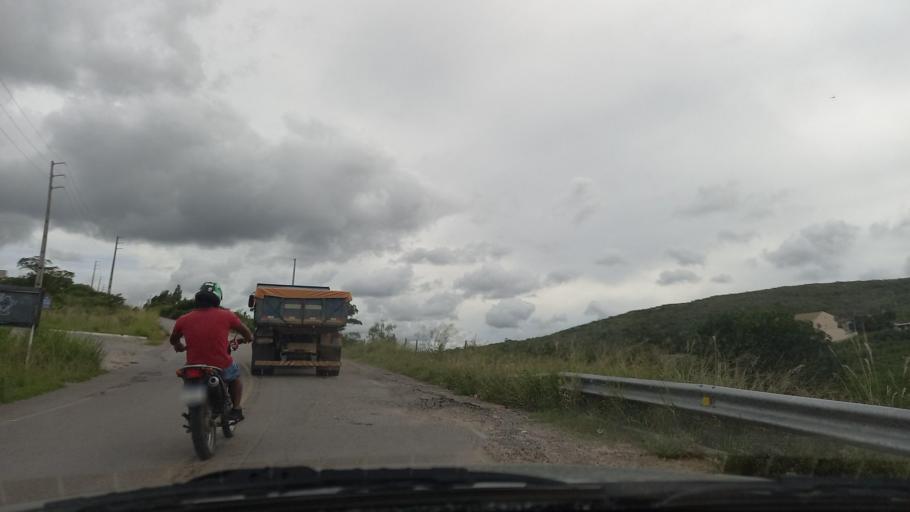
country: BR
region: Pernambuco
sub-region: Gravata
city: Gravata
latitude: -8.2263
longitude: -35.5818
